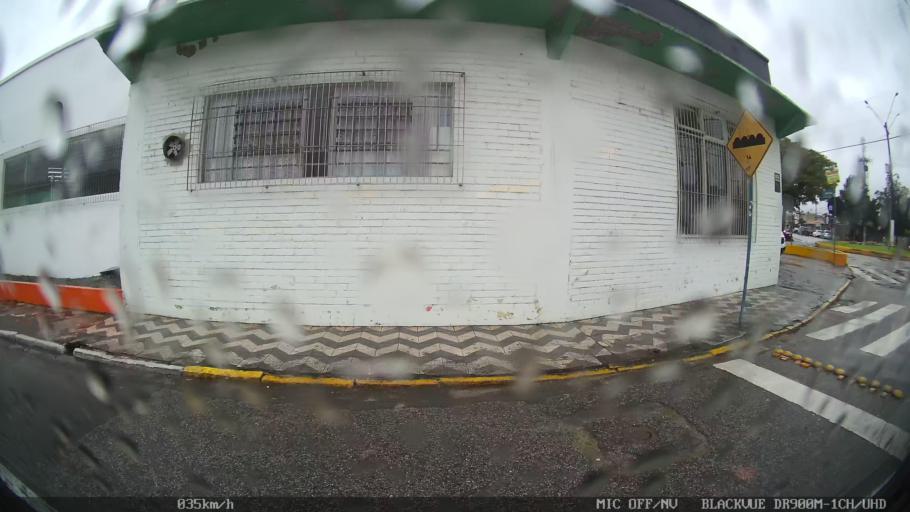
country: BR
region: Santa Catarina
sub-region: Itajai
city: Itajai
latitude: -26.9007
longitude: -48.6774
